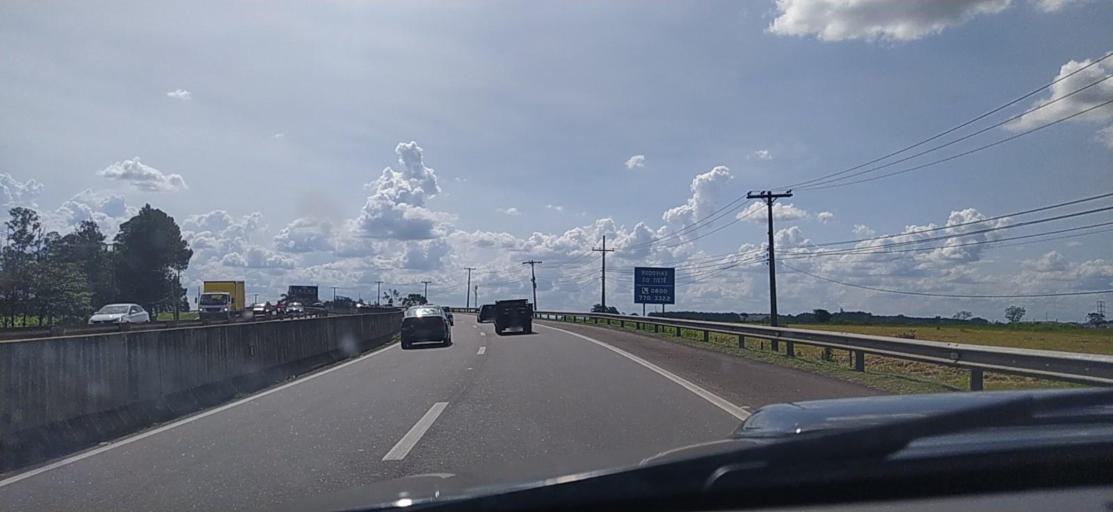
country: BR
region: Sao Paulo
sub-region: Campinas
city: Campinas
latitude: -22.8923
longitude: -47.1267
